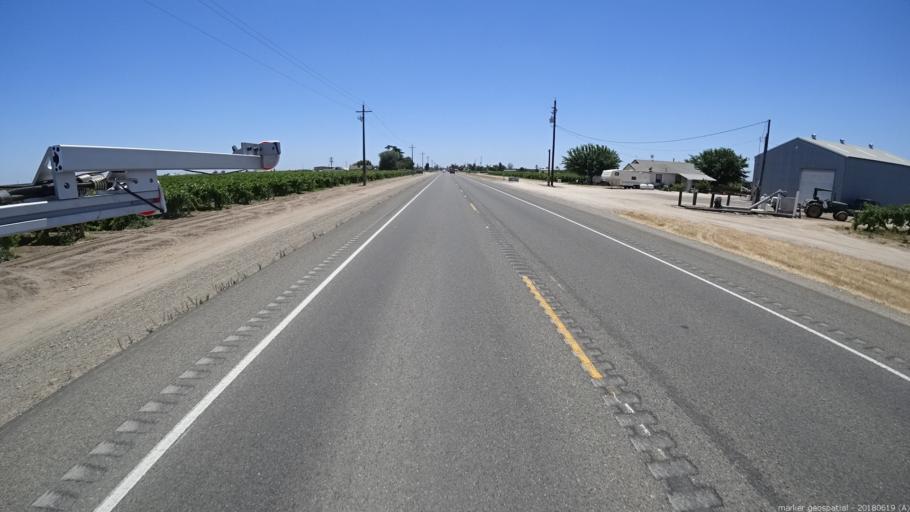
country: US
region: California
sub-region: Madera County
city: Parkwood
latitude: 36.8608
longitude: -120.0557
